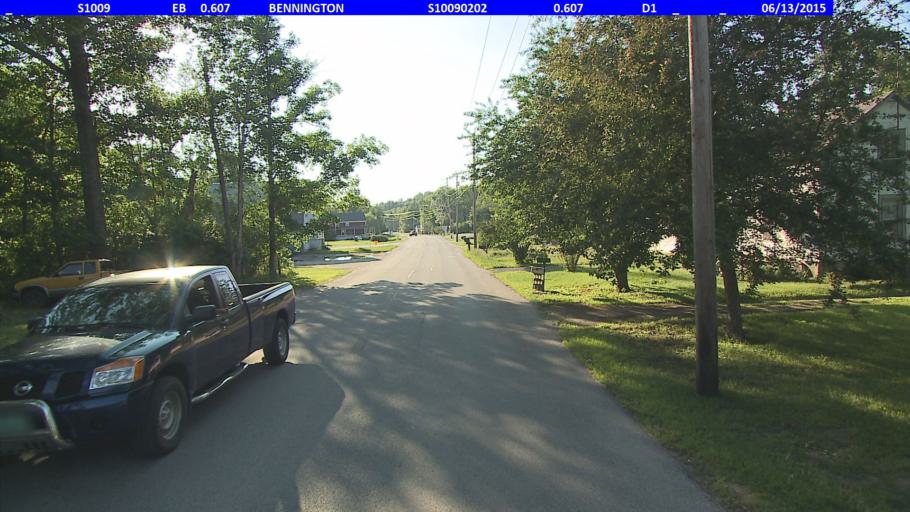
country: US
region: Vermont
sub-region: Bennington County
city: Bennington
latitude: 42.8911
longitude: -73.1829
